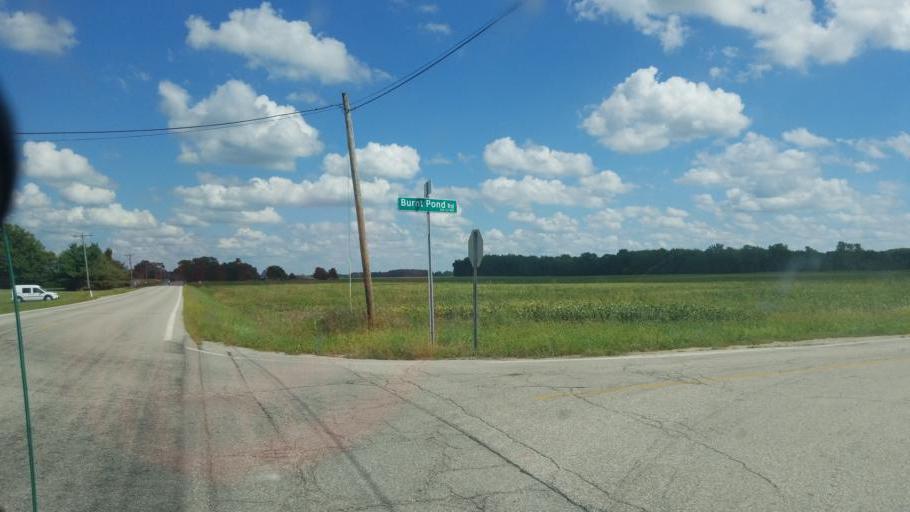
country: US
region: Ohio
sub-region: Union County
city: Richwood
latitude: 40.3377
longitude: -83.2385
